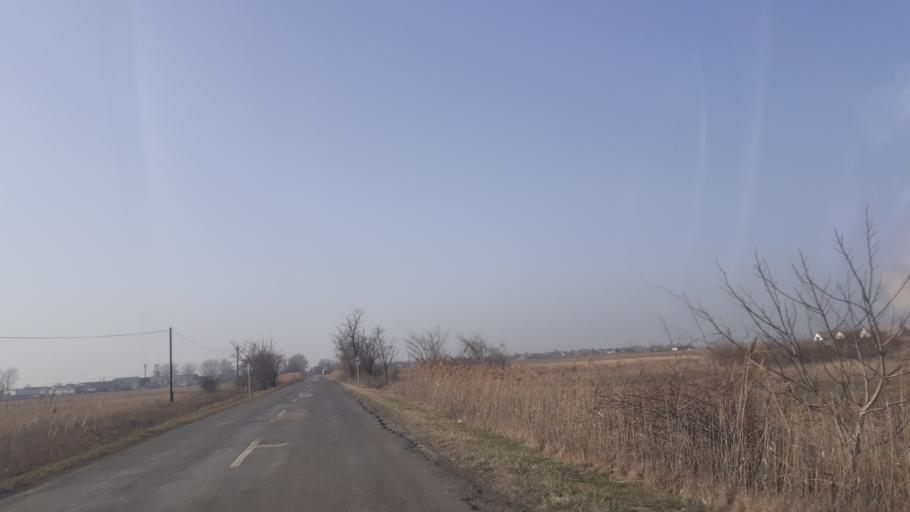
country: HU
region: Bacs-Kiskun
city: Kunszentmiklos
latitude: 47.0252
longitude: 19.1584
